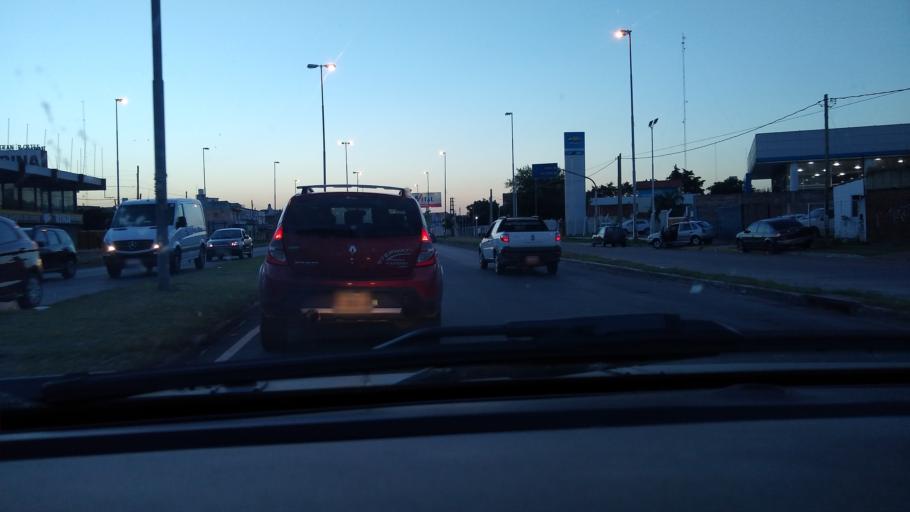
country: AR
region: Buenos Aires
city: San Justo
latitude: -34.6836
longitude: -58.5671
